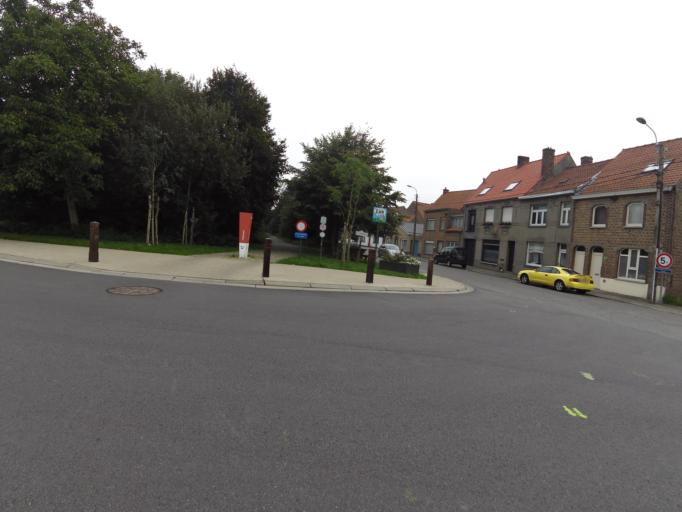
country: BE
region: Flanders
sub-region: Provincie West-Vlaanderen
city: Gistel
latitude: 51.1776
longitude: 2.9391
